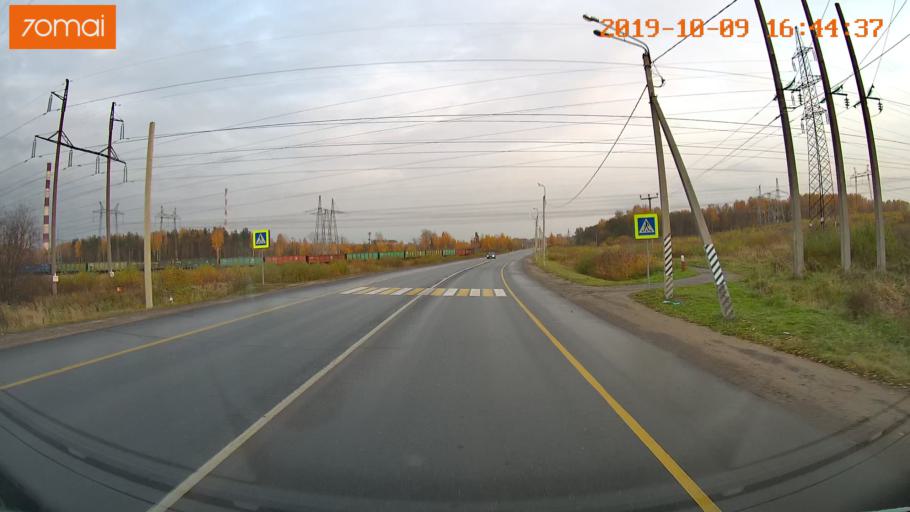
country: RU
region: Kostroma
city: Volgorechensk
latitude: 57.4509
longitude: 41.1436
